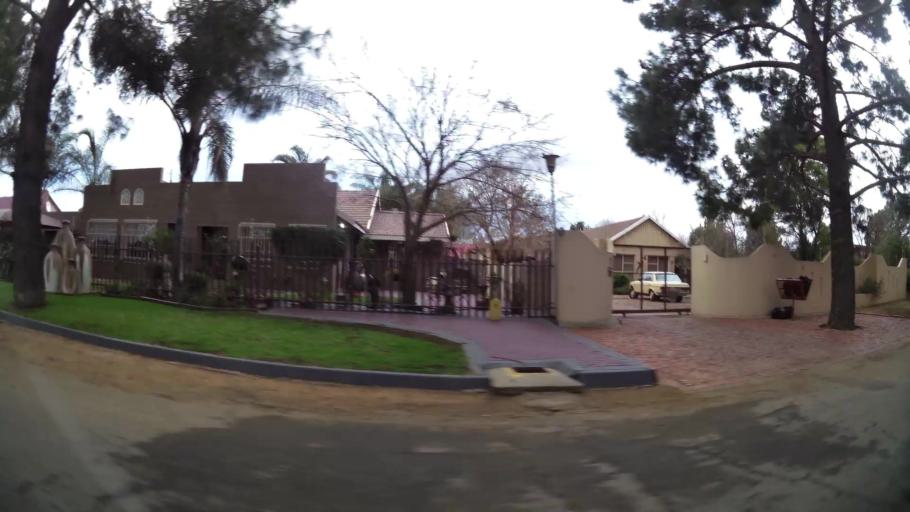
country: ZA
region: Orange Free State
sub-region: Lejweleputswa District Municipality
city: Welkom
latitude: -27.9665
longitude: 26.7249
